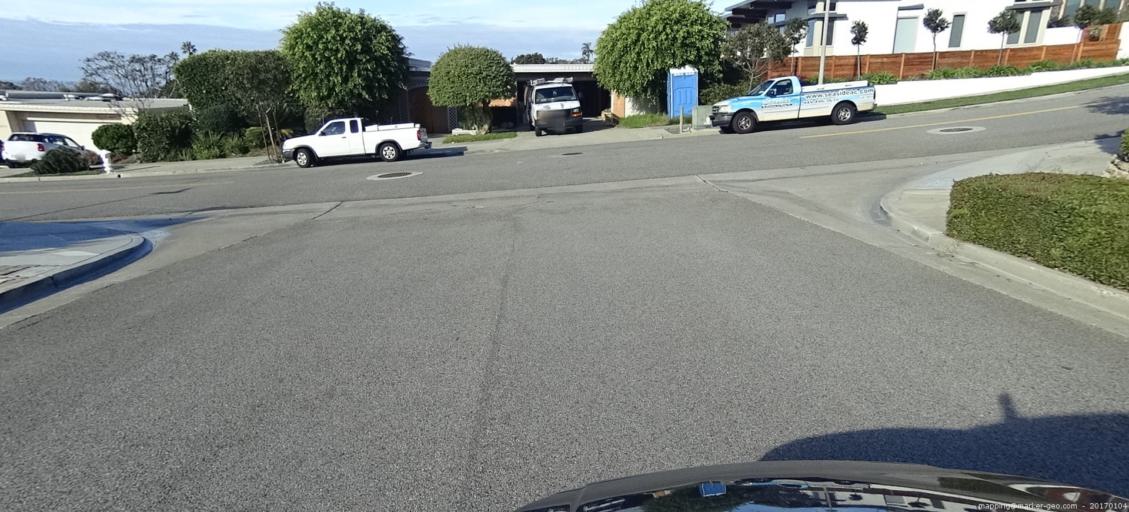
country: US
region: California
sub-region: Orange County
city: Laguna Niguel
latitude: 33.4919
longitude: -117.7288
